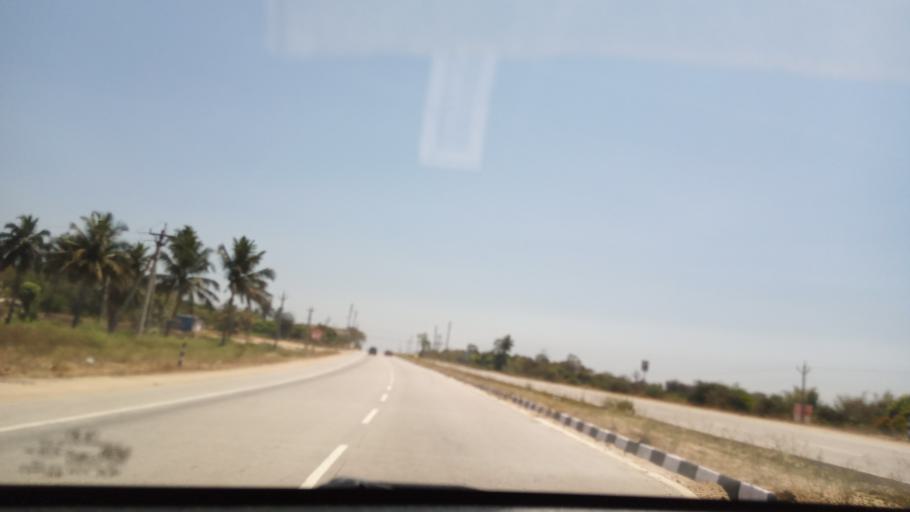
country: IN
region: Andhra Pradesh
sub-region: Chittoor
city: Chittoor
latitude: 13.1983
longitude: 78.9750
